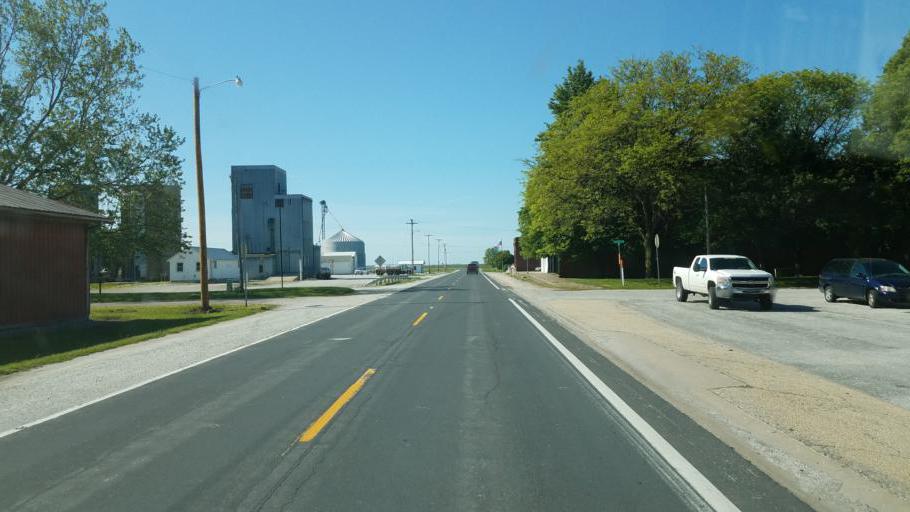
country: US
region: Illinois
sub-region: McDonough County
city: Bushnell
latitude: 40.4194
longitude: -90.4969
